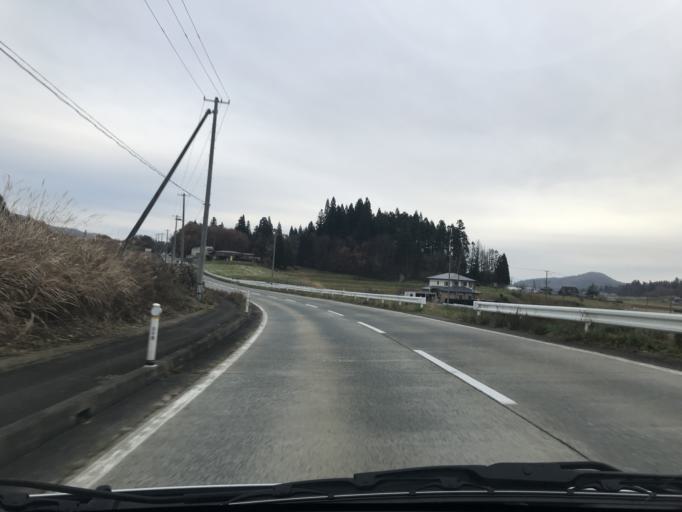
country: JP
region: Iwate
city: Kitakami
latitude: 39.2913
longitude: 141.2129
